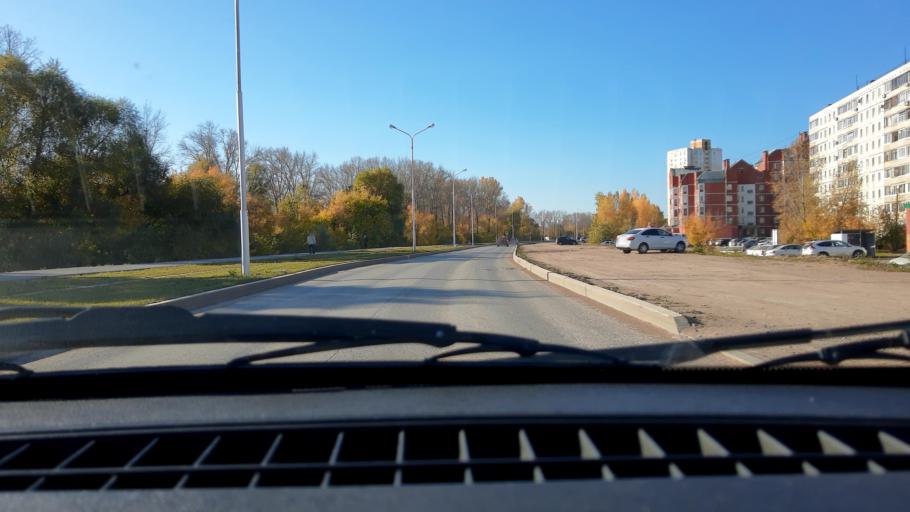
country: RU
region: Bashkortostan
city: Ufa
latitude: 54.7683
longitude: 56.0834
